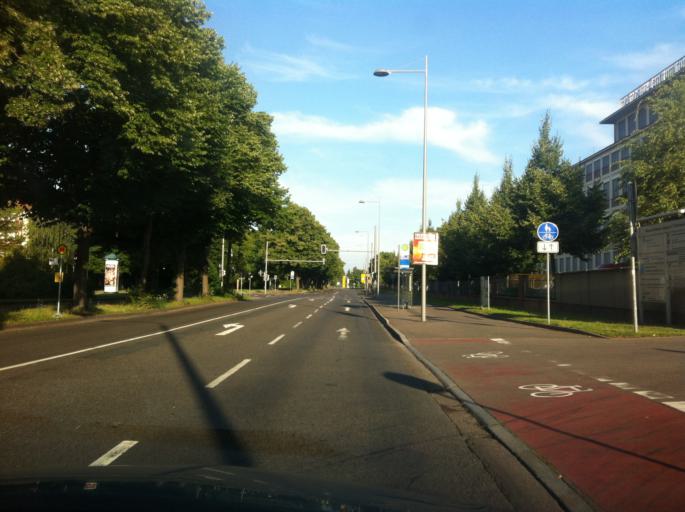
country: DE
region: Saxony
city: Taucha
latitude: 51.3513
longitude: 12.4318
